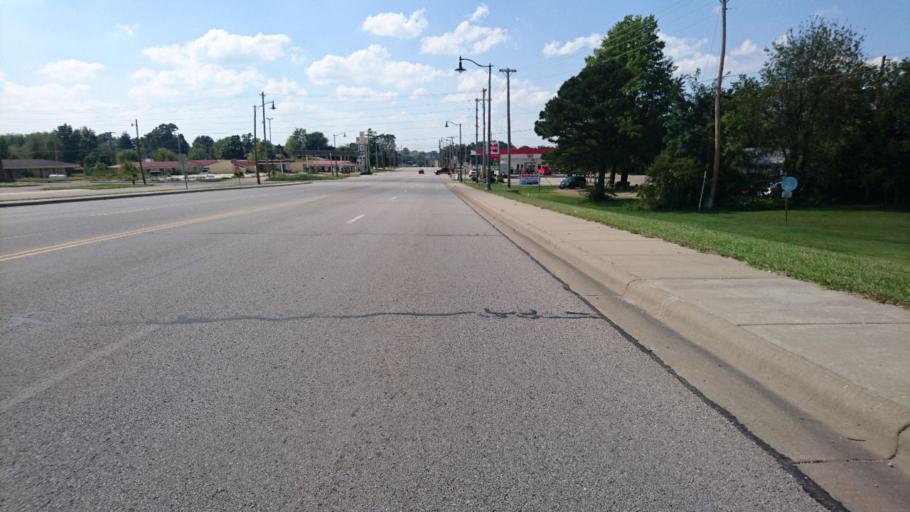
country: US
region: Missouri
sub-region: Laclede County
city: Lebanon
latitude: 37.6838
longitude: -92.6439
